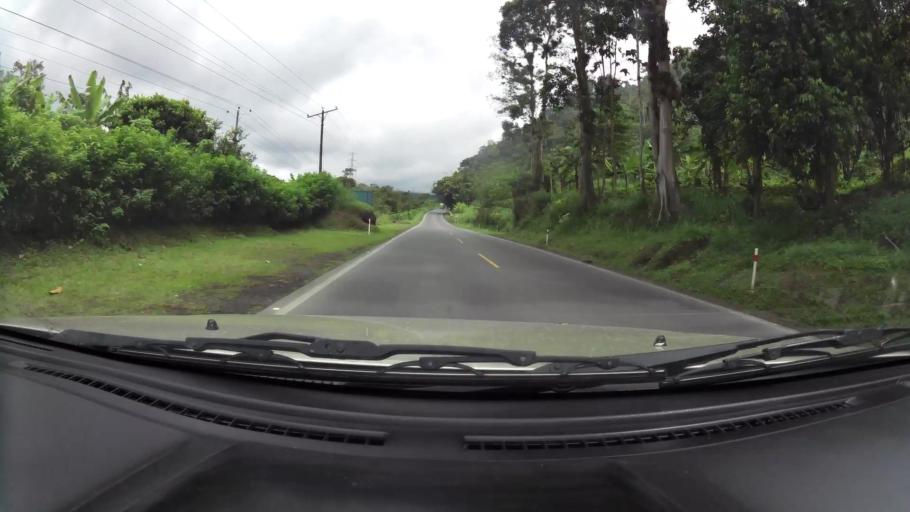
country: EC
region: Santo Domingo de los Tsachilas
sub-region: Canton Santo Domingo de los Colorados
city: Santo Domingo de los Colorados
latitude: -0.3045
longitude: -79.0441
